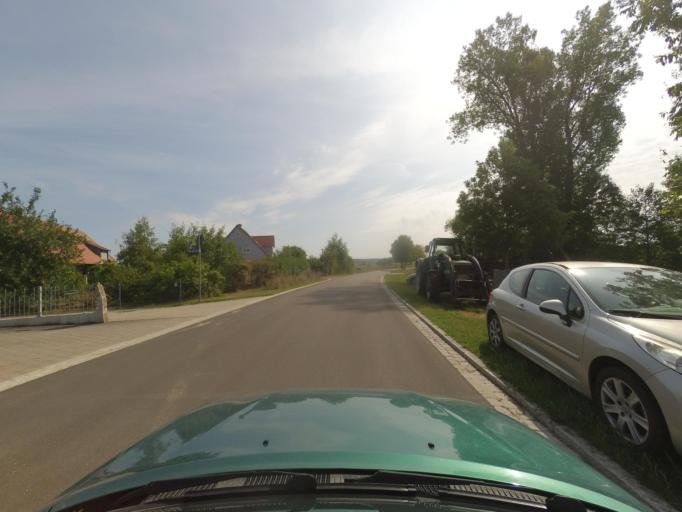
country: DE
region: Bavaria
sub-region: Regierungsbezirk Mittelfranken
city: Herrieden
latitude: 49.2260
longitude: 10.5164
